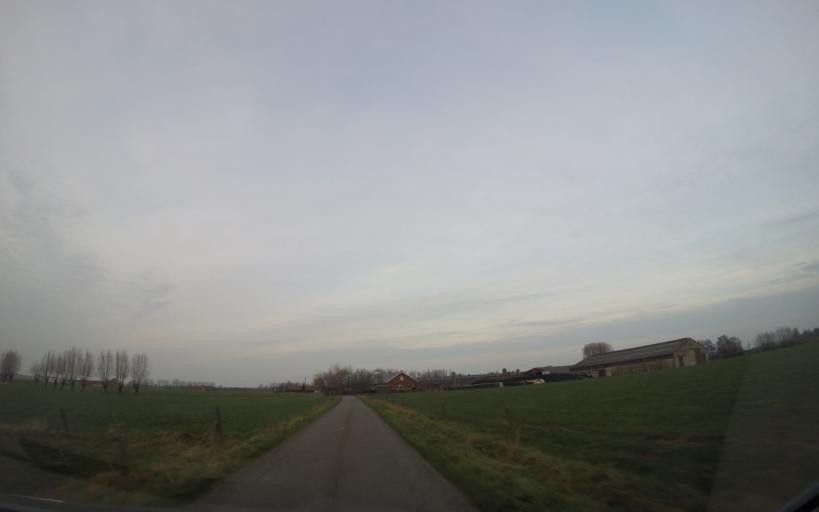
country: BE
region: Flanders
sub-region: Provincie West-Vlaanderen
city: Ruiselede
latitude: 51.0281
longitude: 3.4131
